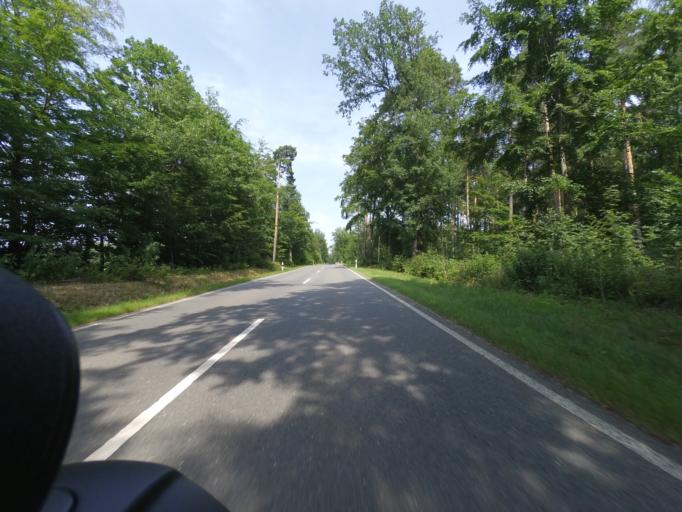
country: DE
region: Thuringia
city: Tautenhain
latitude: 50.9132
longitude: 11.9001
